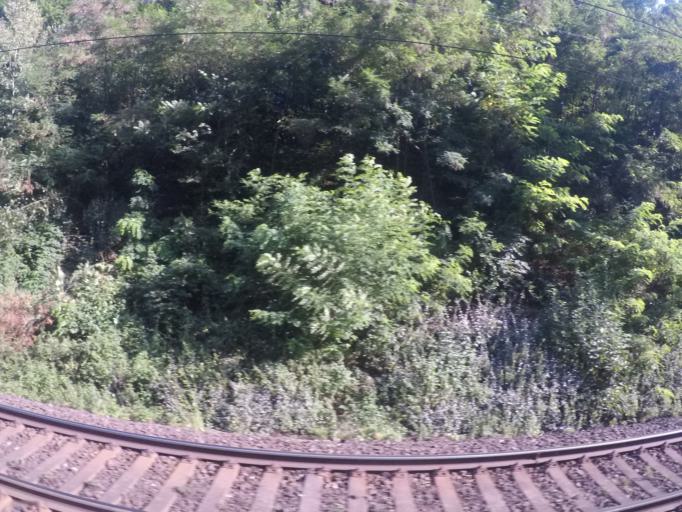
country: SK
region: Presovsky
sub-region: Okres Presov
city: Presov
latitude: 48.8652
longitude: 21.2023
